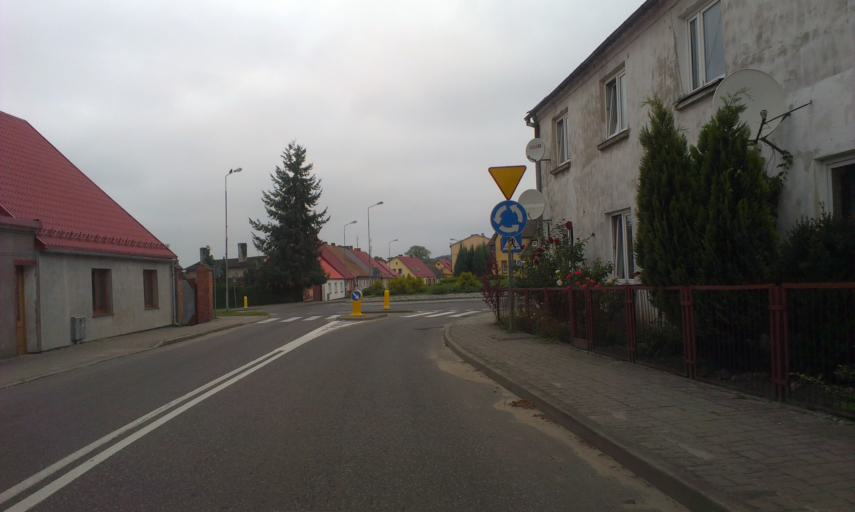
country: PL
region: West Pomeranian Voivodeship
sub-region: Powiat szczecinecki
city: Barwice
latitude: 53.7375
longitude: 16.3547
